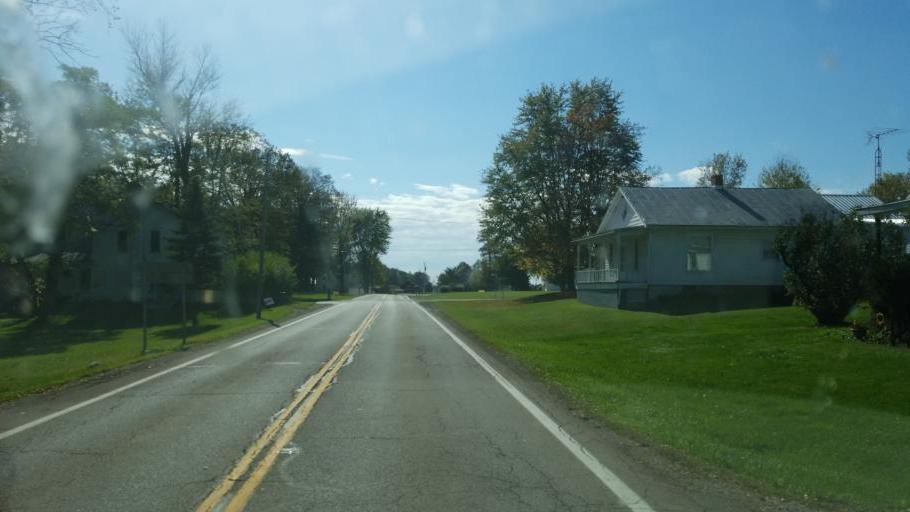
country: US
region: Ohio
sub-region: Morrow County
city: Mount Gilead
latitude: 40.5789
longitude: -82.7308
